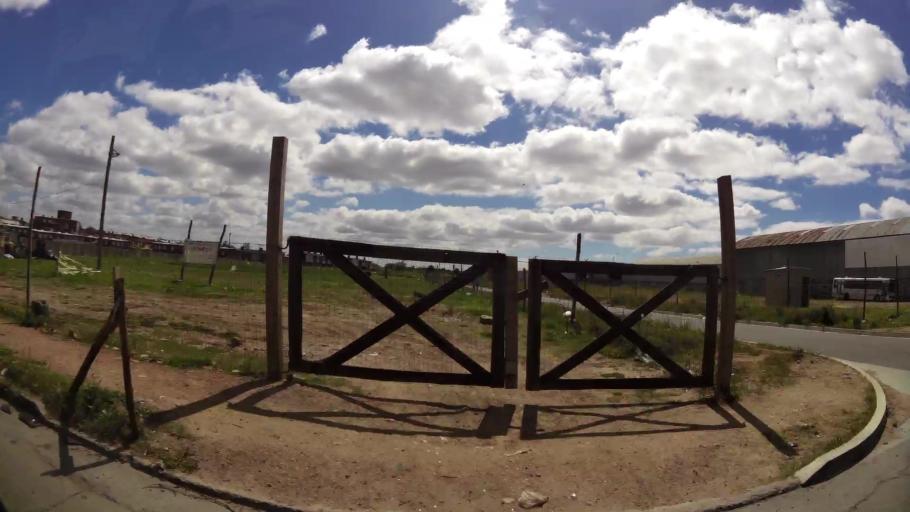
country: UY
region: Canelones
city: Paso de Carrasco
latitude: -34.8625
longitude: -56.1231
